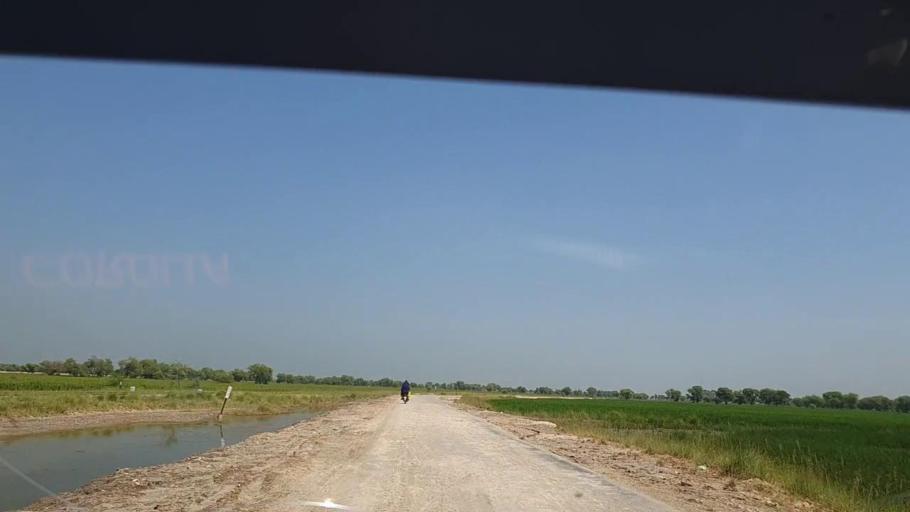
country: PK
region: Sindh
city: Tangwani
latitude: 28.2841
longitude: 69.0224
